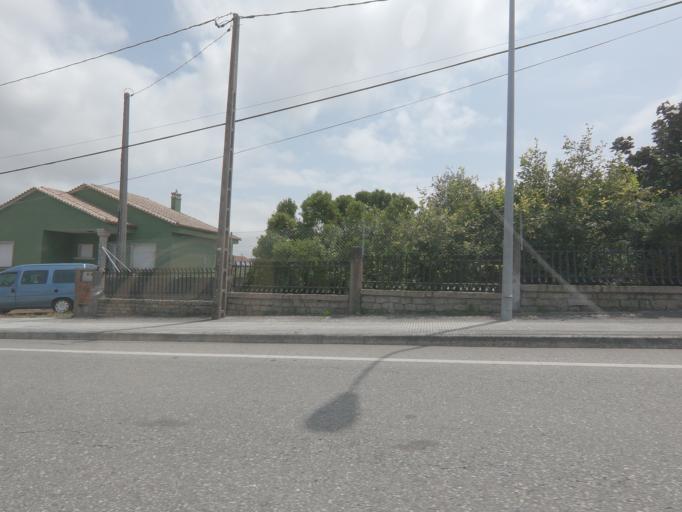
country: ES
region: Galicia
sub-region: Provincia de Pontevedra
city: A Guarda
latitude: 41.9077
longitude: -8.8605
